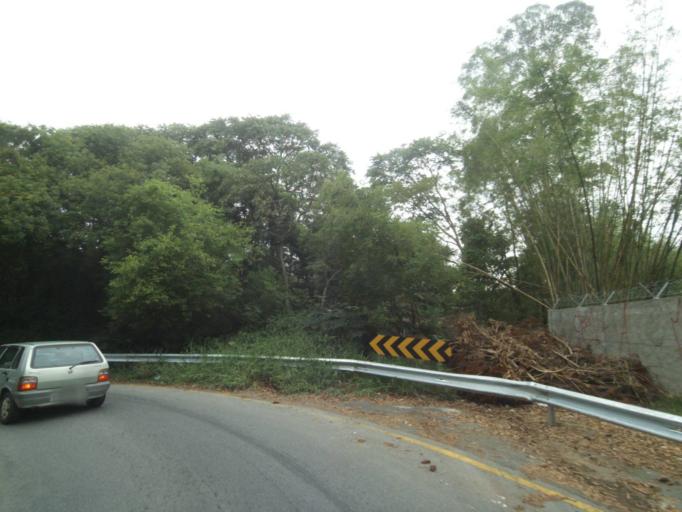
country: BR
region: Parana
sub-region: Curitiba
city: Curitiba
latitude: -25.4055
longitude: -49.3058
